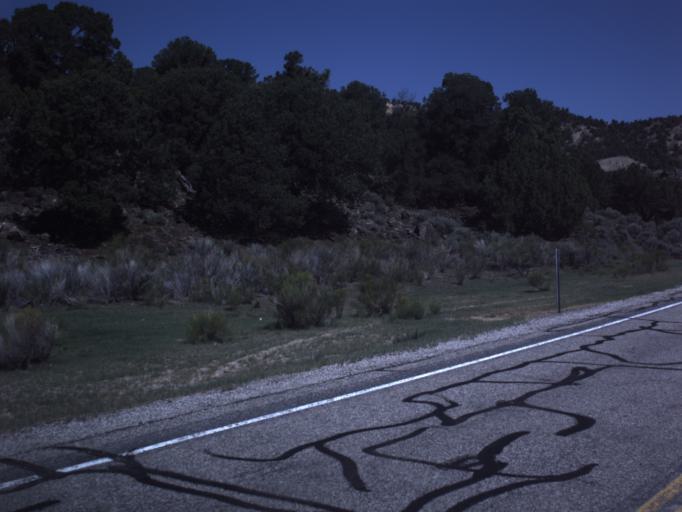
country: US
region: Utah
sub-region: Wayne County
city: Loa
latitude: 38.6836
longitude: -111.3976
